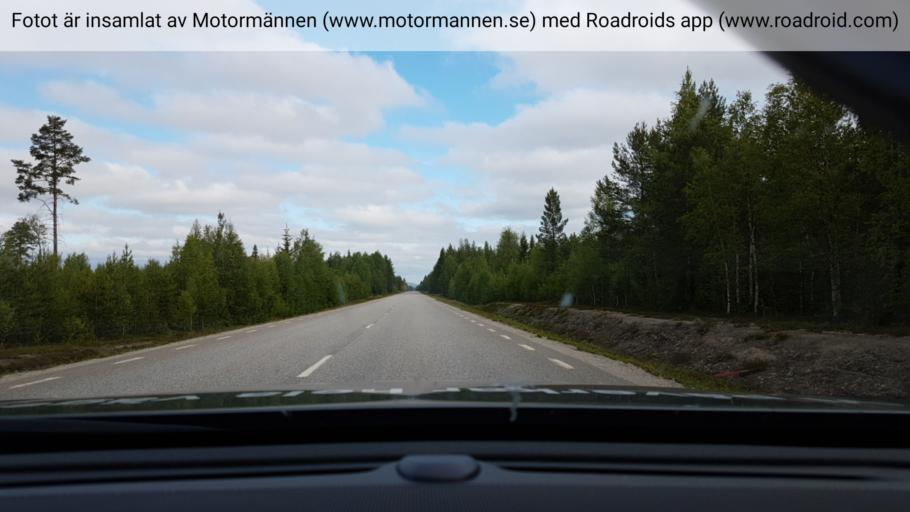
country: SE
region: Vaesterbotten
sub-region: Norsjo Kommun
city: Norsjoe
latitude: 64.5521
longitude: 19.3266
